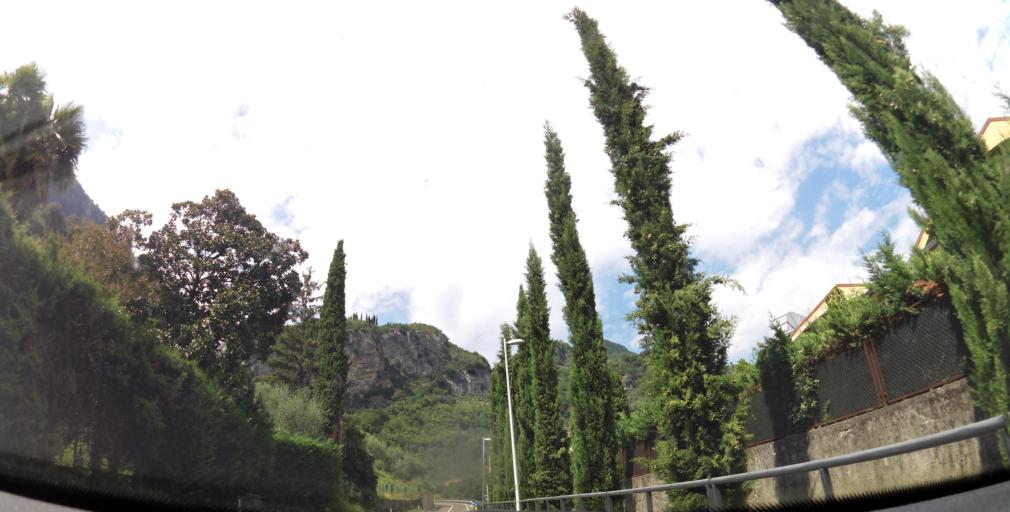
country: IT
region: Trentino-Alto Adige
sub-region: Provincia di Trento
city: Tenno
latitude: 45.9091
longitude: 10.8383
